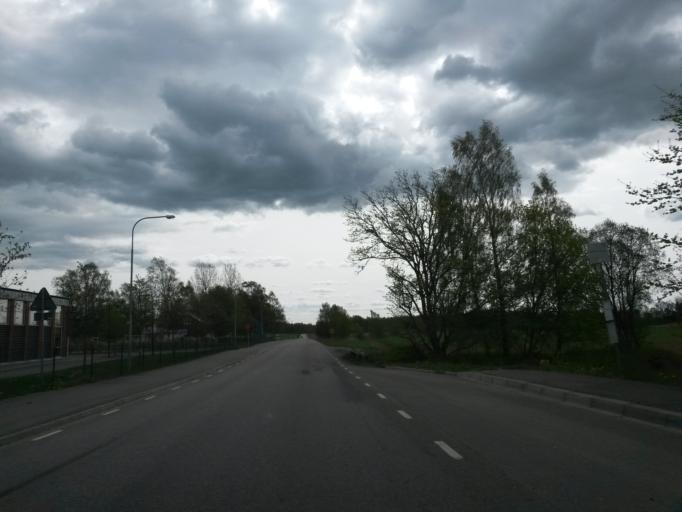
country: SE
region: Vaestra Goetaland
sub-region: Herrljunga Kommun
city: Herrljunga
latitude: 58.1688
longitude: 12.9999
